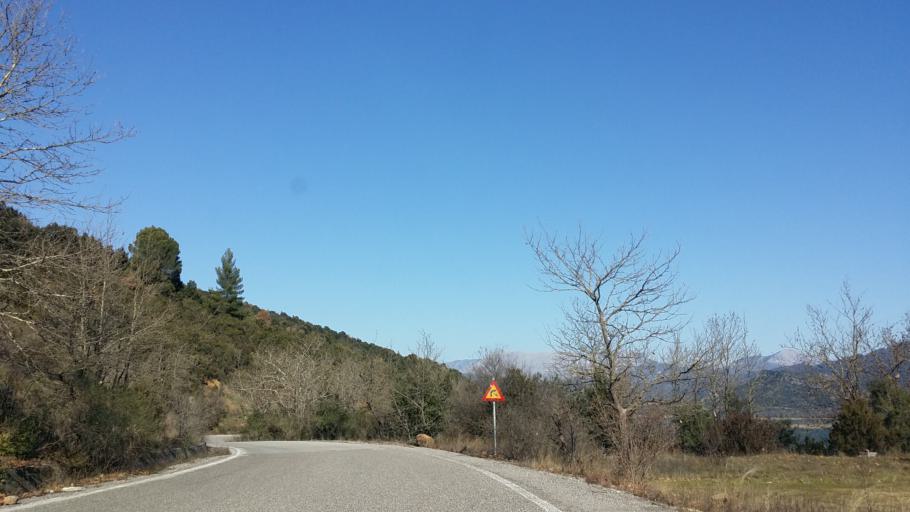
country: GR
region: West Greece
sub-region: Nomos Aitolias kai Akarnanias
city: Lepenou
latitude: 38.8040
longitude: 21.3328
